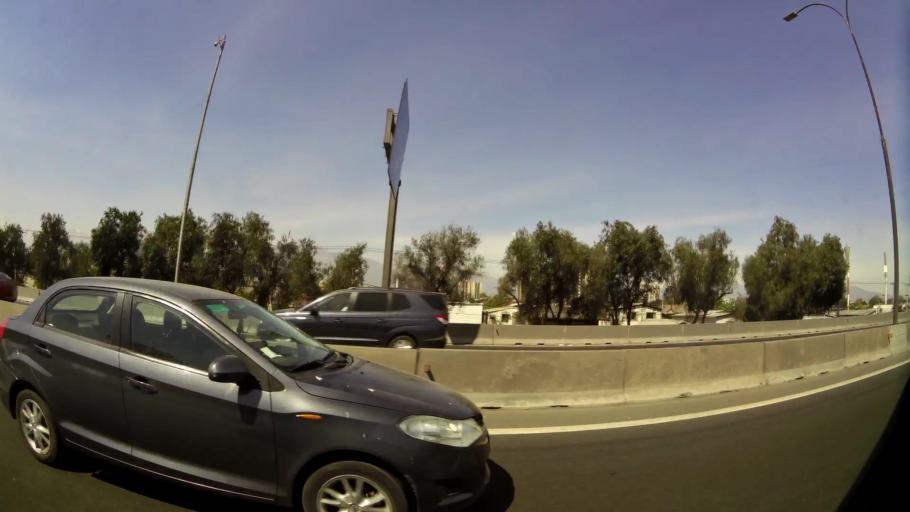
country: CL
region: Santiago Metropolitan
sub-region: Provincia de Santiago
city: Santiago
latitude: -33.5102
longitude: -70.6708
